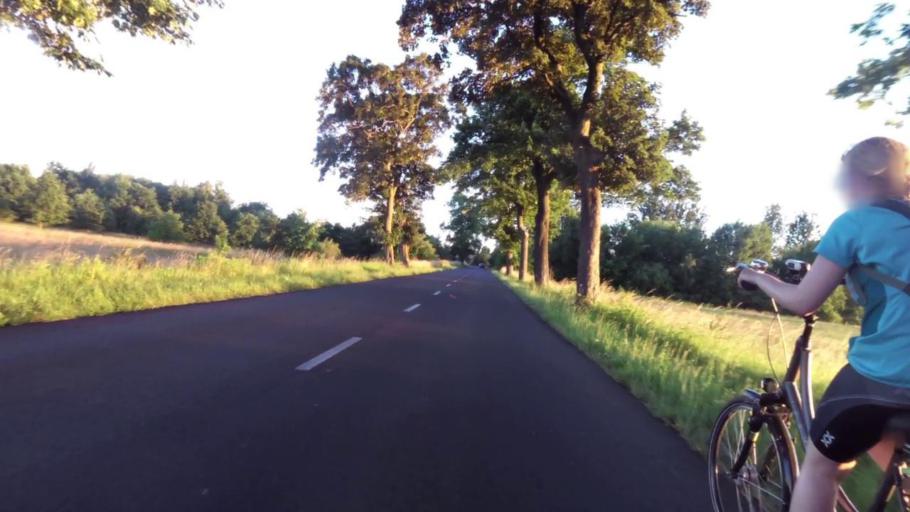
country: PL
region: West Pomeranian Voivodeship
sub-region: Powiat bialogardzki
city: Bialogard
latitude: 54.0163
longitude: 16.0088
